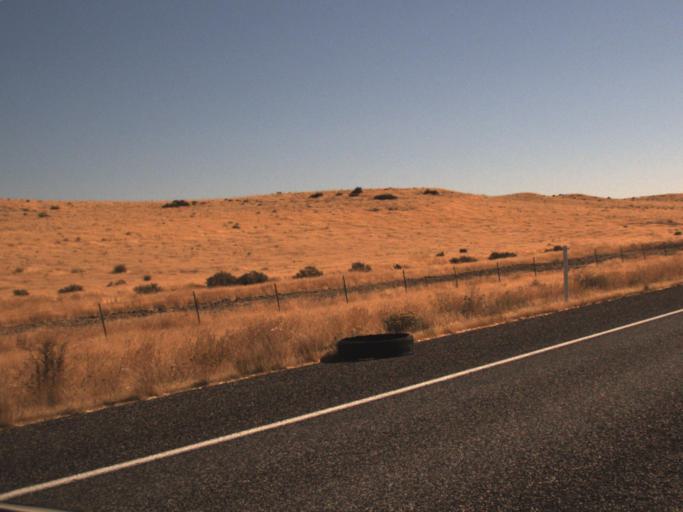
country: US
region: Washington
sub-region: Benton County
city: Benton City
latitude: 46.4502
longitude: -119.5058
